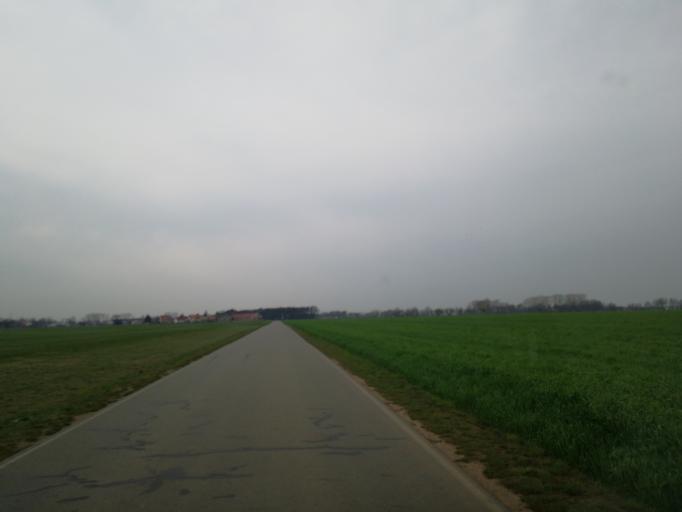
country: DE
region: Brandenburg
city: Elsterwerda
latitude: 51.4419
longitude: 13.4695
